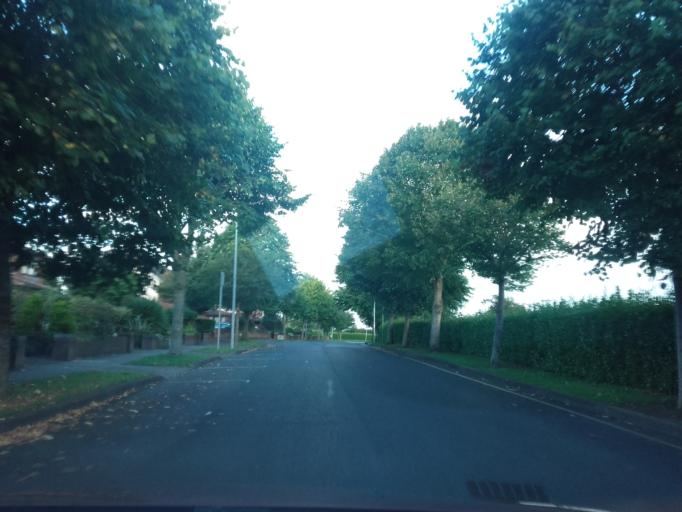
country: IE
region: Leinster
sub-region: Fingal County
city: Swords
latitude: 53.4549
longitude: -6.2278
